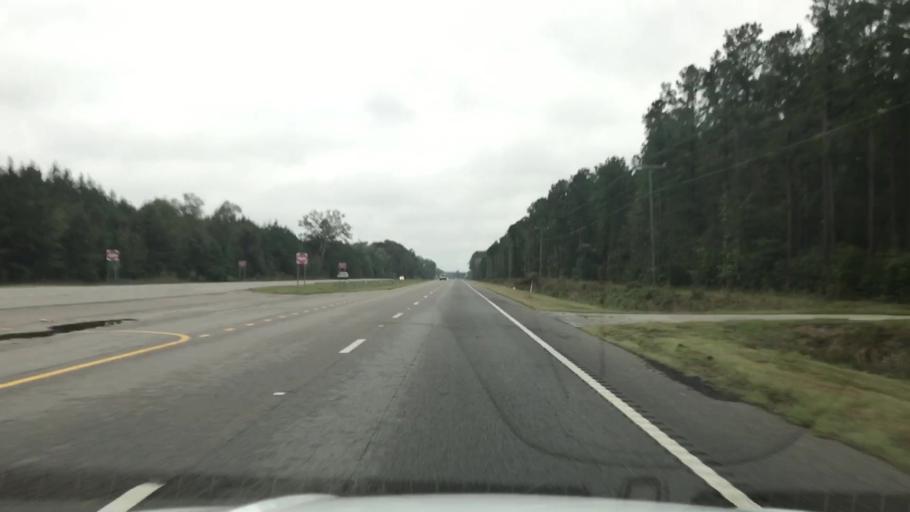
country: US
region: South Carolina
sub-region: Colleton County
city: Walterboro
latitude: 32.6909
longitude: -80.6285
